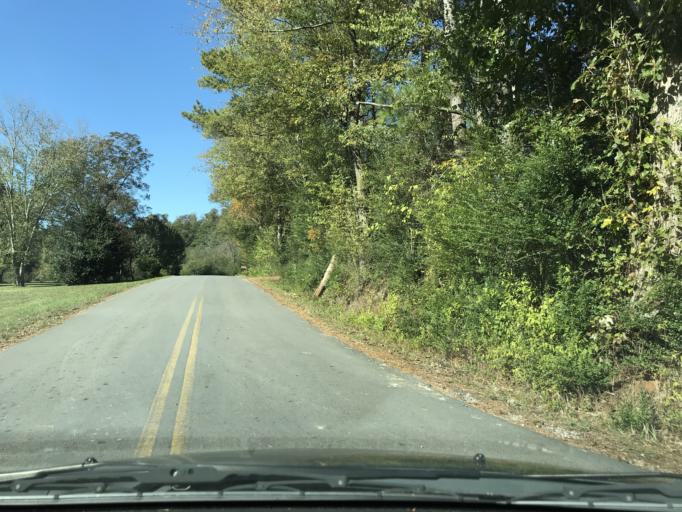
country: US
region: Georgia
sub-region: Dade County
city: Trenton
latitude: 34.9018
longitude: -85.4614
